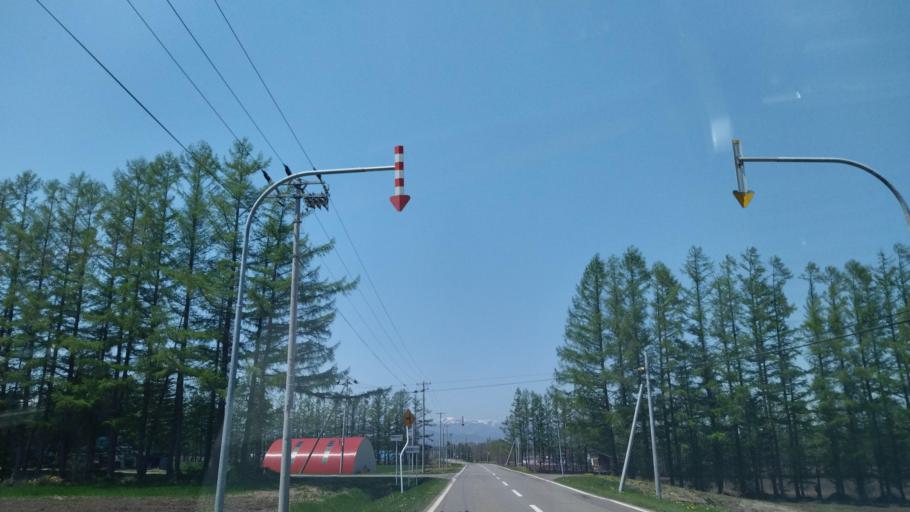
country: JP
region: Hokkaido
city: Obihiro
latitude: 42.9080
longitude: 142.9917
